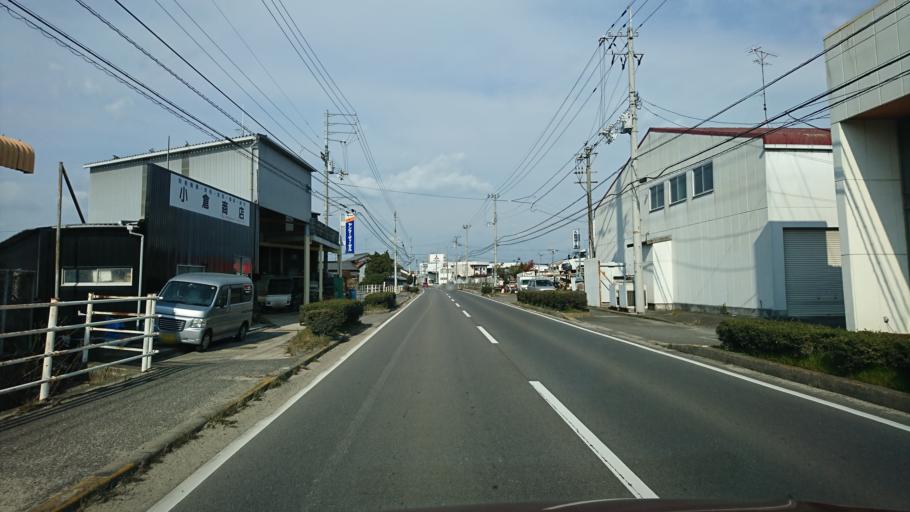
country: JP
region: Ehime
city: Saijo
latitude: 34.0116
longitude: 133.0387
